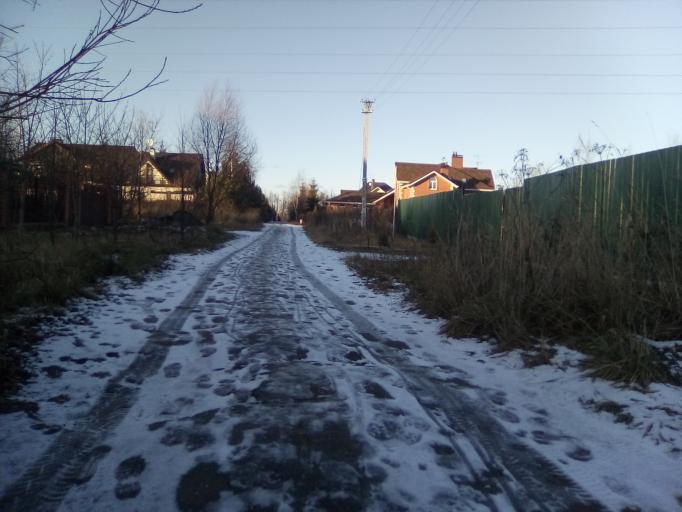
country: RU
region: Moskovskaya
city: Lesnoy Gorodok
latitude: 55.6487
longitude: 37.1592
